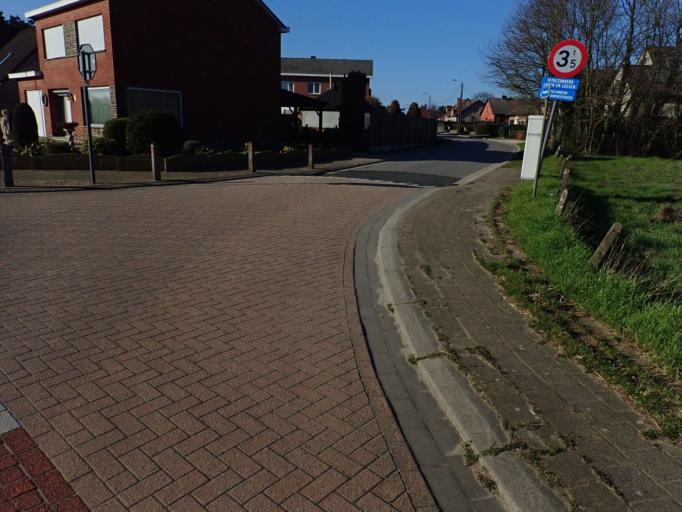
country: BE
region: Flanders
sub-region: Provincie Antwerpen
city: Olen
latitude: 51.1225
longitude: 4.8356
